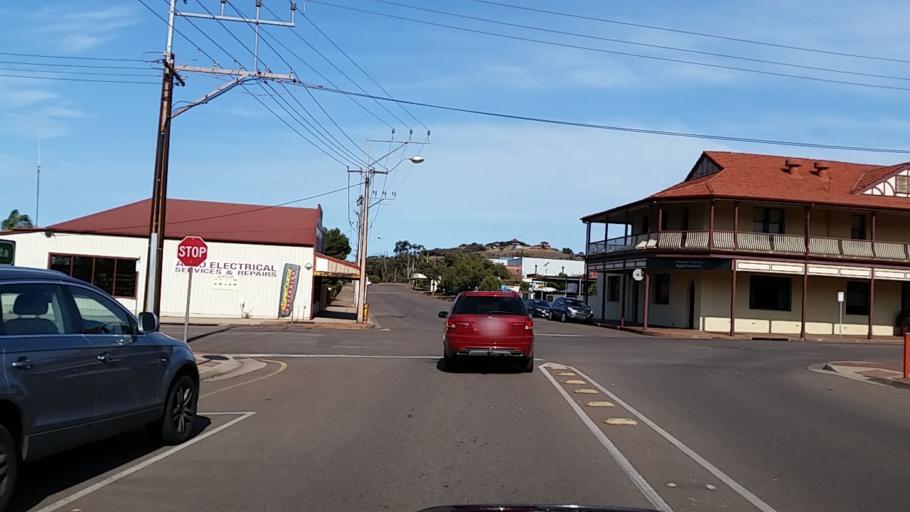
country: AU
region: South Australia
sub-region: Whyalla
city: Whyalla
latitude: -33.0337
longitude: 137.5859
